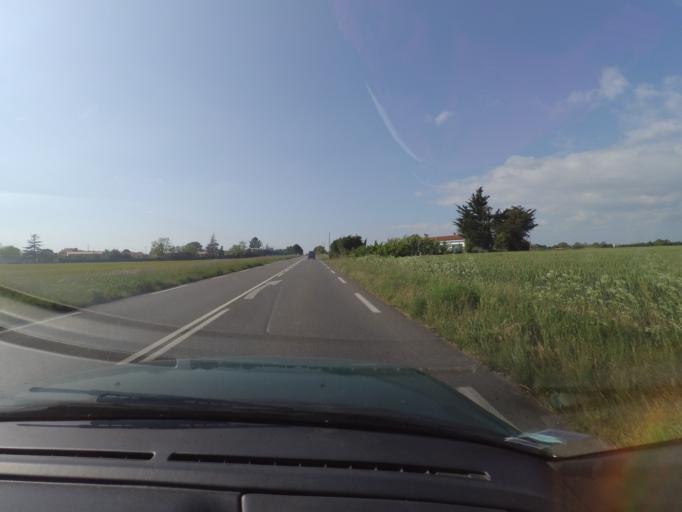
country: FR
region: Pays de la Loire
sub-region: Departement de la Vendee
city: Angles
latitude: 46.4223
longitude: -1.3931
